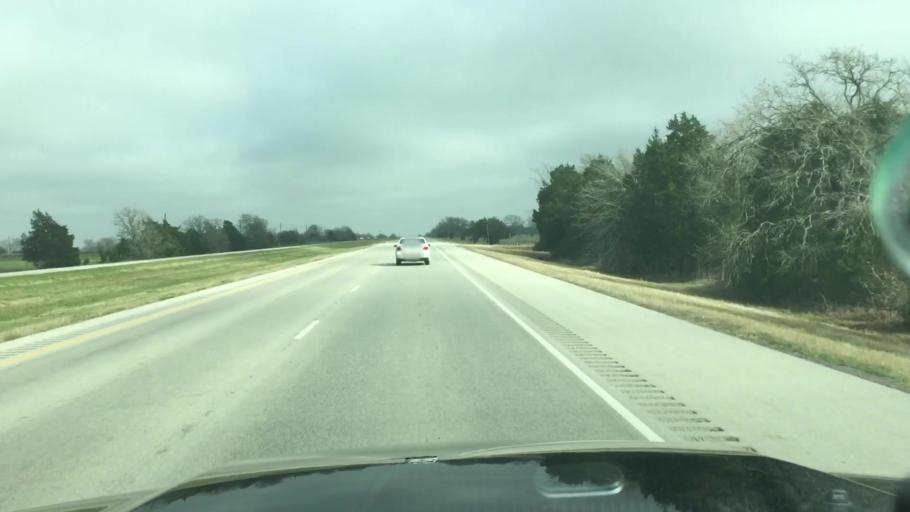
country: US
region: Texas
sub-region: Lee County
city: Giddings
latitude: 30.1443
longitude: -96.7304
